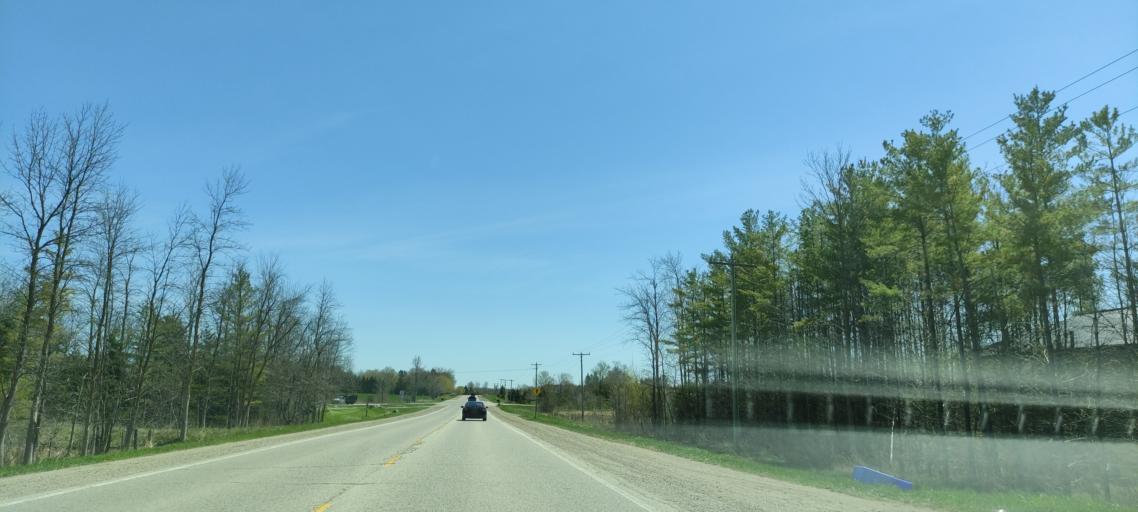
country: CA
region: Ontario
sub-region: Wellington County
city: Guelph
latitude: 43.5751
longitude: -80.3822
